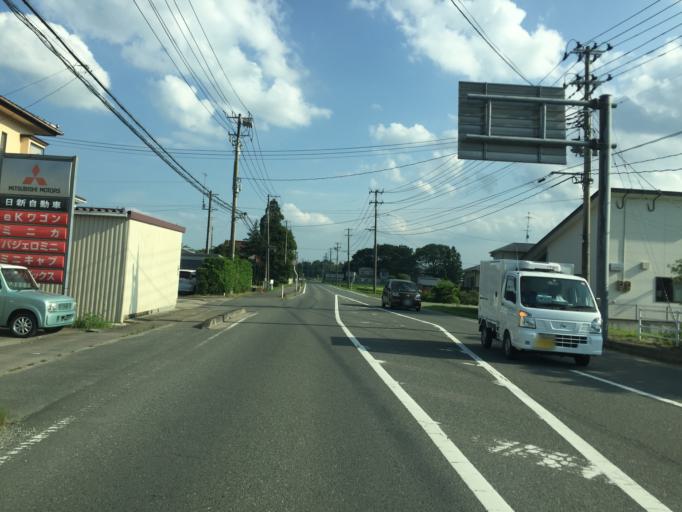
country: JP
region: Miyagi
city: Marumori
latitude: 37.7850
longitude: 140.9141
